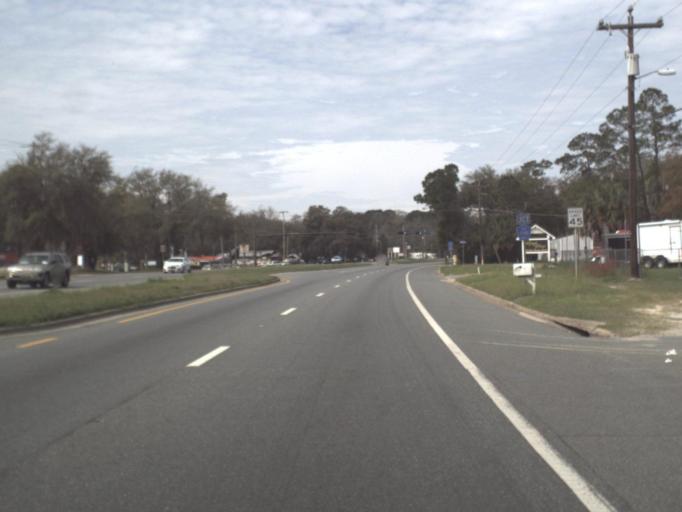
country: US
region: Florida
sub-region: Gadsden County
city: Midway
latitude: 30.4563
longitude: -84.3719
